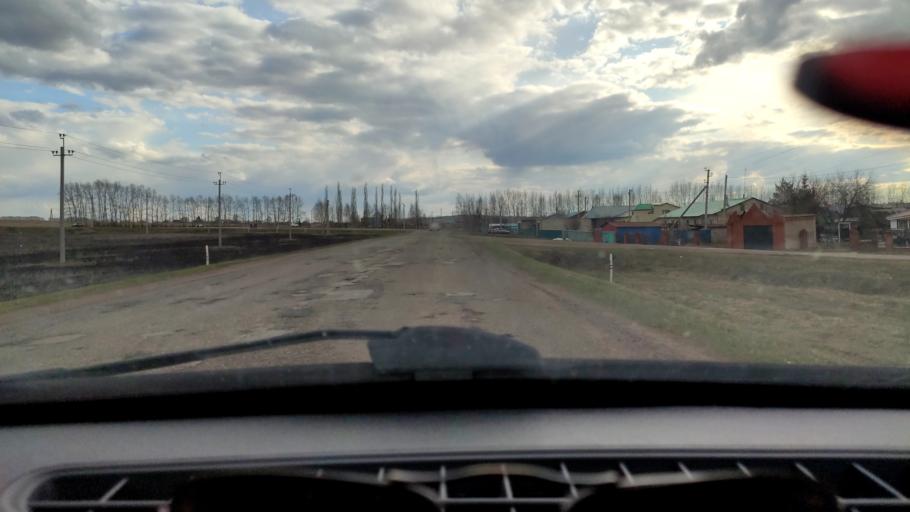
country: RU
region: Bashkortostan
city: Karmaskaly
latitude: 54.3919
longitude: 56.2402
